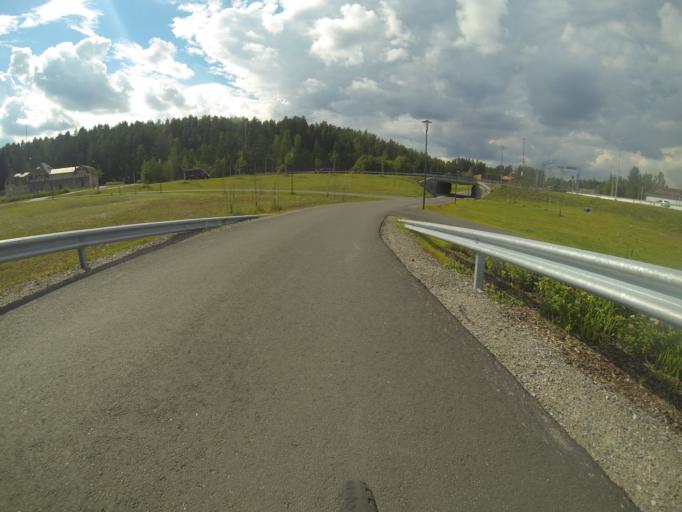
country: FI
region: Southern Savonia
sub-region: Savonlinna
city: Savonlinna
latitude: 61.8758
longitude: 28.8759
